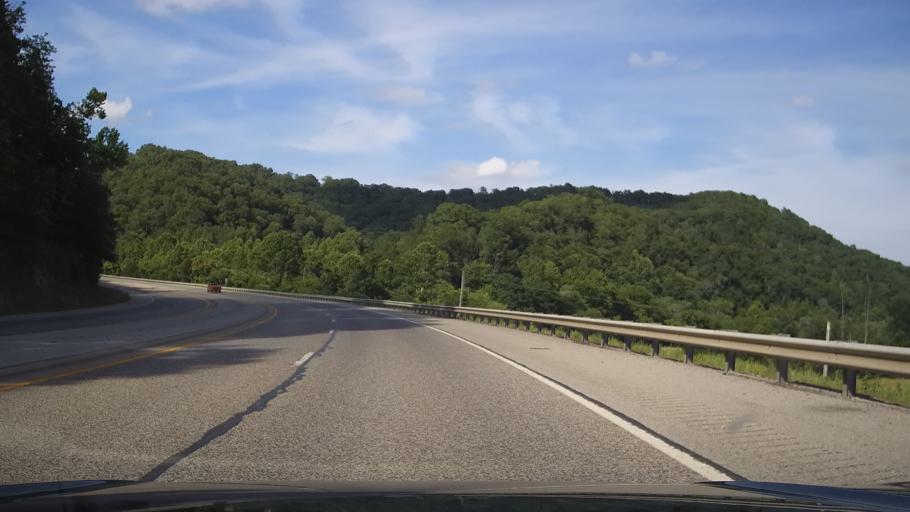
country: US
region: Kentucky
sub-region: Lawrence County
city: Louisa
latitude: 38.0206
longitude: -82.6526
